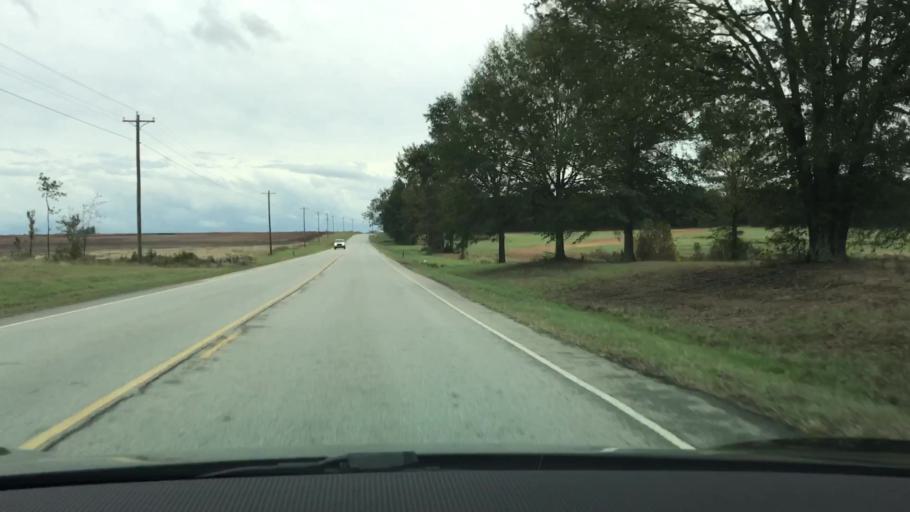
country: US
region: Georgia
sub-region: Jefferson County
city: Wrens
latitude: 33.1158
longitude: -82.4365
